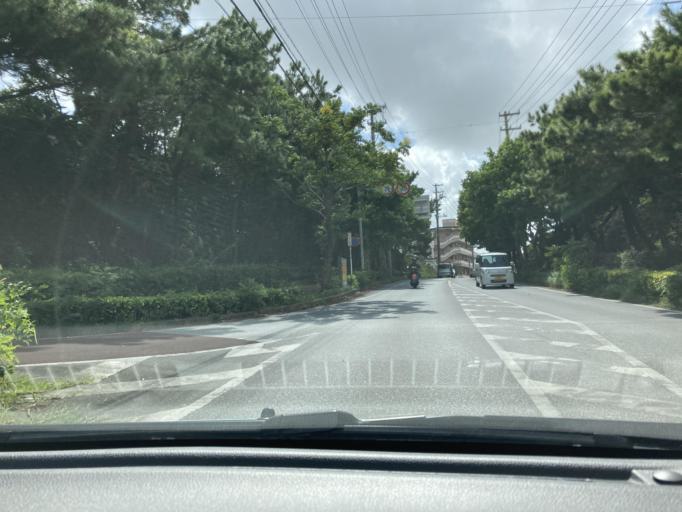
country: JP
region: Okinawa
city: Ginowan
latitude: 26.2570
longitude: 127.7241
